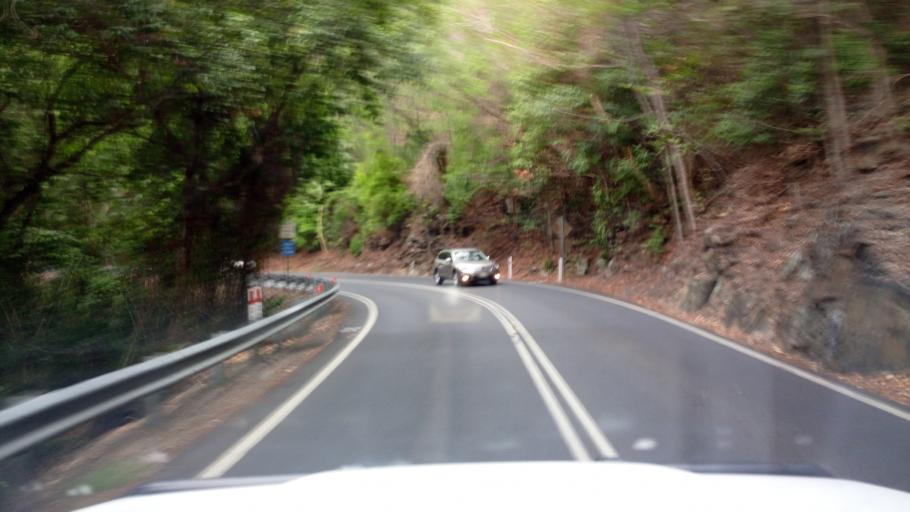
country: AU
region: Queensland
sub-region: Cairns
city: Redlynch
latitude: -16.8478
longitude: 145.6829
